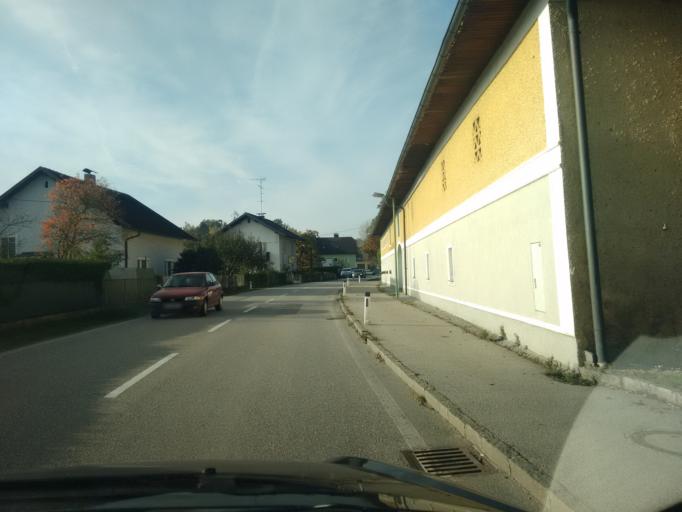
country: AT
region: Upper Austria
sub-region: Wels Stadt
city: Wels
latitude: 48.1777
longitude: 13.9845
